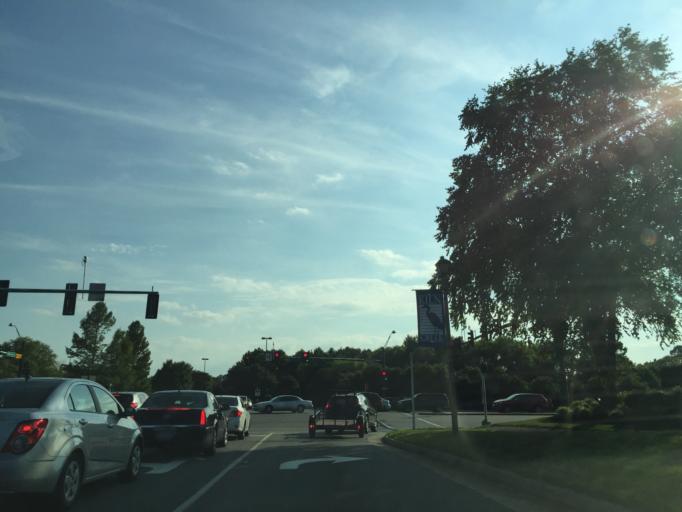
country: US
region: Virginia
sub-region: York County
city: Yorktown
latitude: 37.1216
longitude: -76.5059
